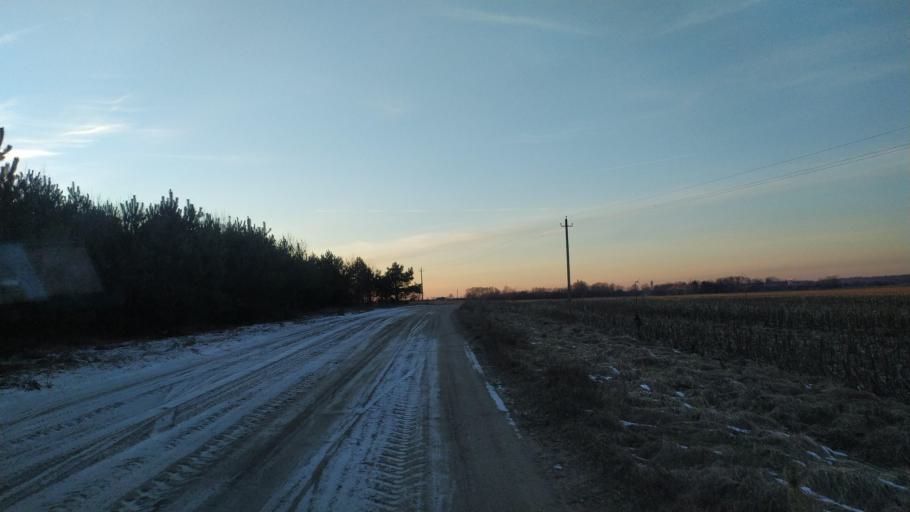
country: BY
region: Brest
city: Pruzhany
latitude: 52.5473
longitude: 24.2402
